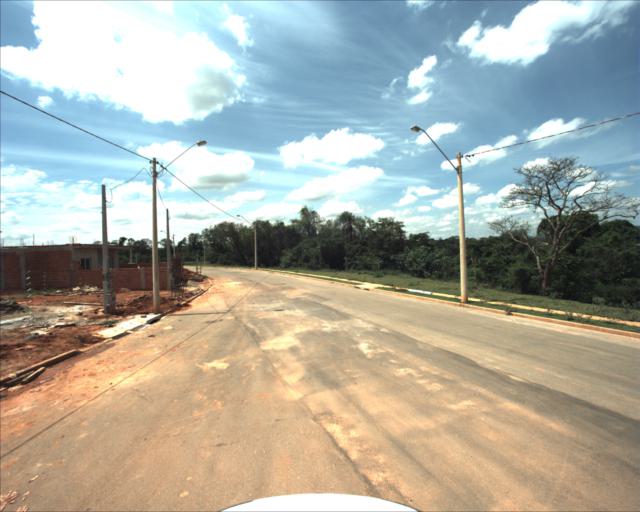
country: BR
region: Sao Paulo
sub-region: Sorocaba
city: Sorocaba
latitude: -23.4086
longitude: -47.4048
